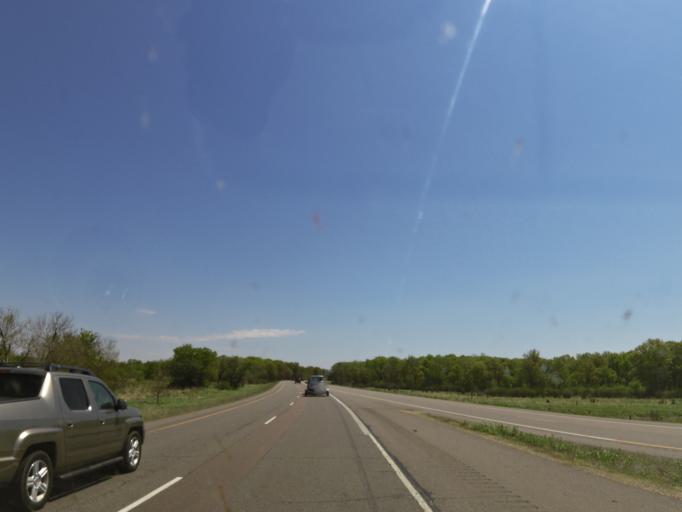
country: US
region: Wisconsin
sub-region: Monroe County
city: Tomah
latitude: 43.9833
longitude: -90.4416
